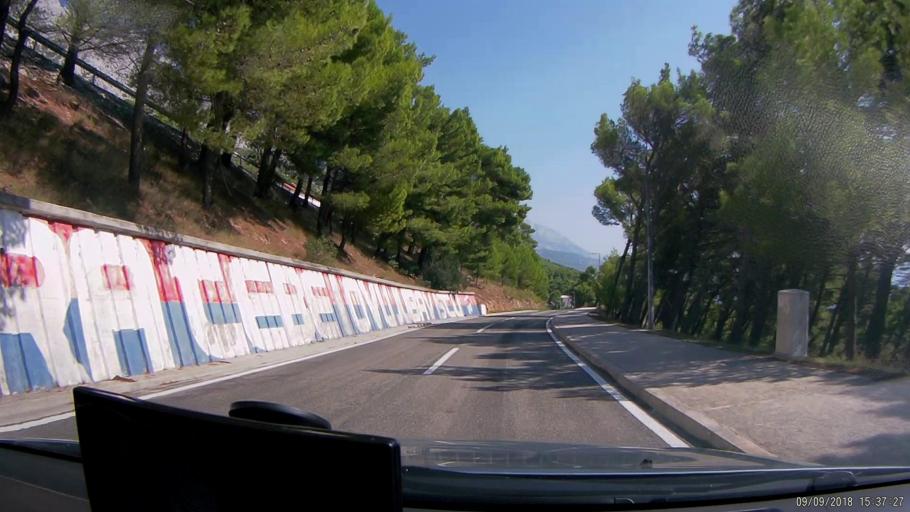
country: HR
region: Splitsko-Dalmatinska
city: Donja Brela
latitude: 43.3729
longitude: 16.9285
